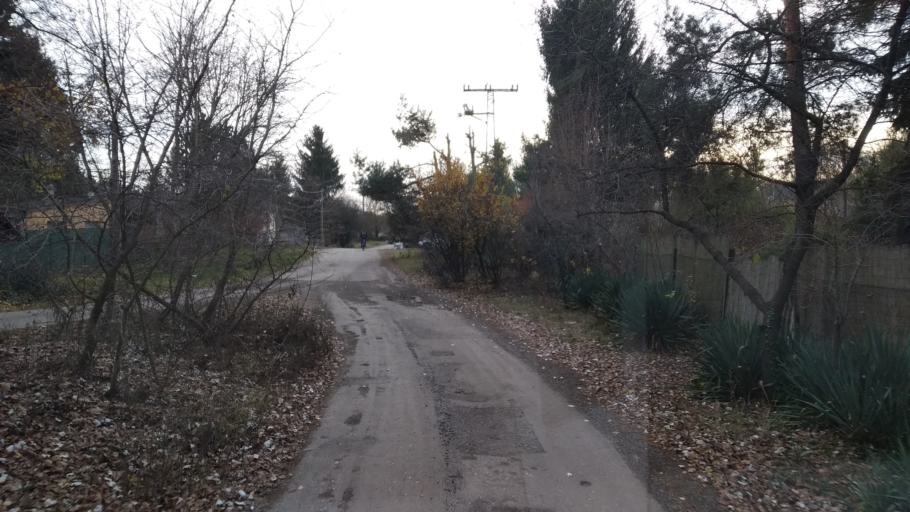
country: HU
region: Pest
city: God
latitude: 47.6761
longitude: 19.1112
